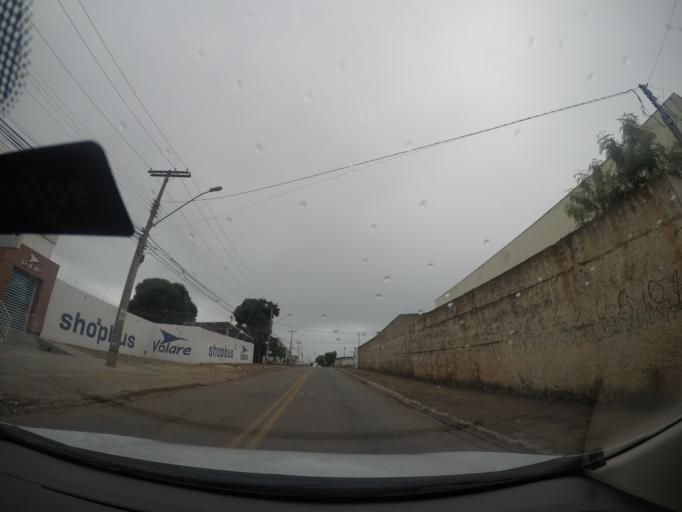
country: BR
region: Goias
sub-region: Goiania
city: Goiania
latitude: -16.6541
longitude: -49.3175
